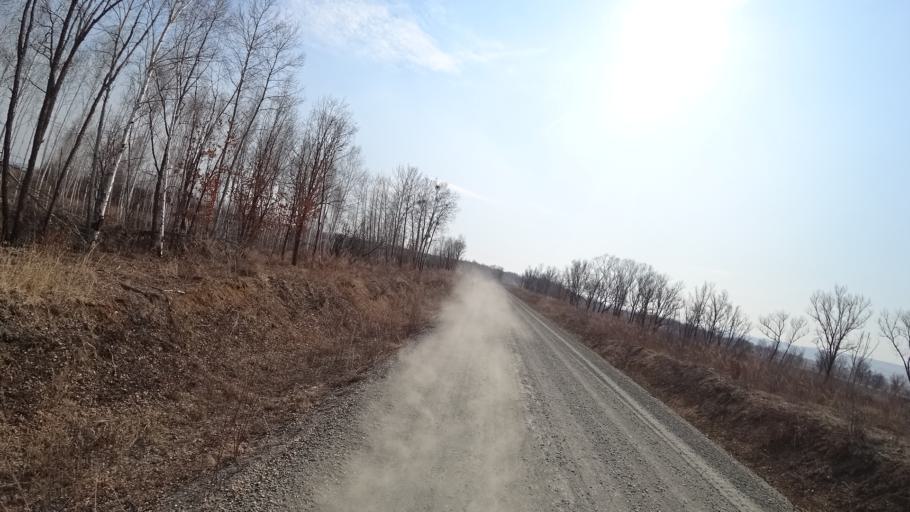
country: RU
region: Amur
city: Novobureyskiy
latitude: 49.8258
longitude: 129.9874
